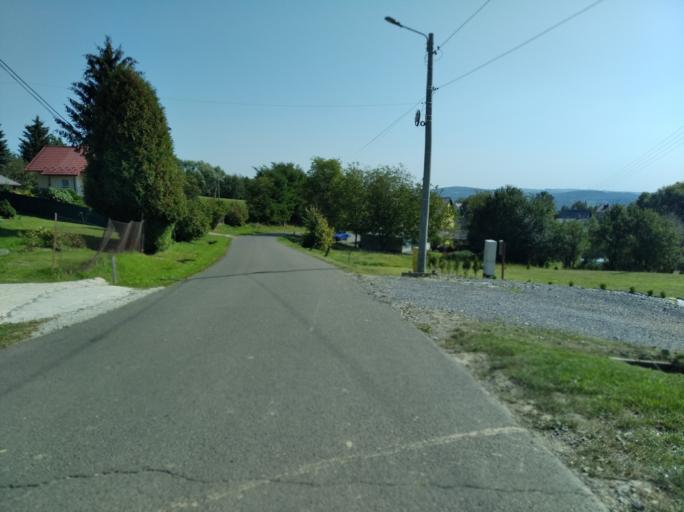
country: PL
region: Subcarpathian Voivodeship
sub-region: Powiat strzyzowski
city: Czudec
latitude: 49.9527
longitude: 21.8316
